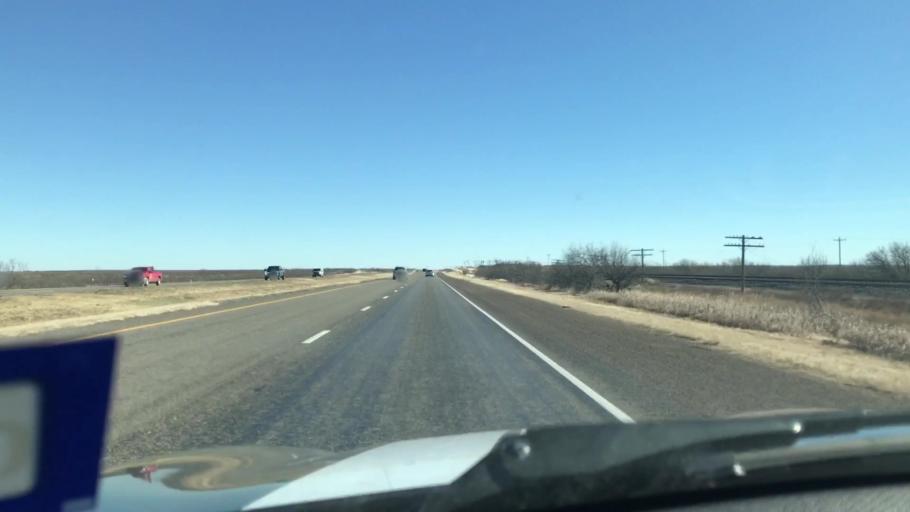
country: US
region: Texas
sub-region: Garza County
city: Post
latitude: 33.1290
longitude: -101.2973
